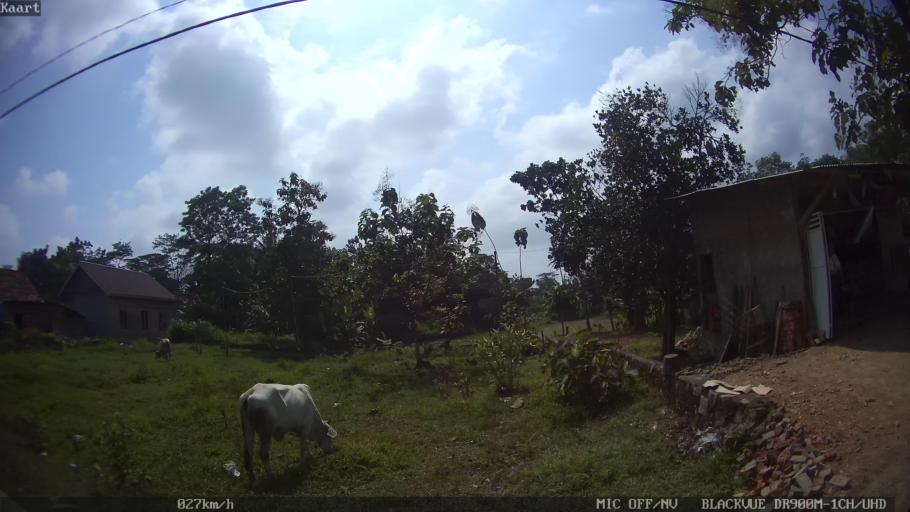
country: ID
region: Lampung
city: Kedaton
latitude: -5.3305
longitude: 105.2726
